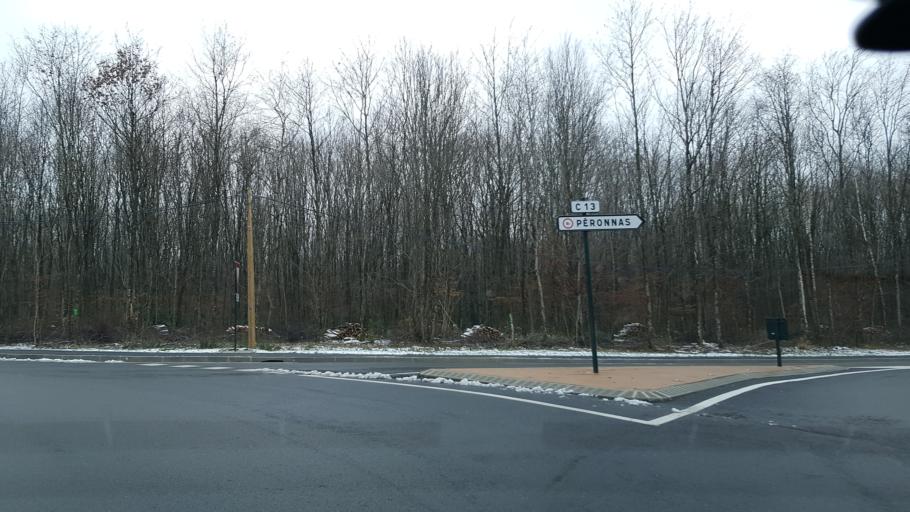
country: FR
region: Rhone-Alpes
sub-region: Departement de l'Ain
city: Peronnas
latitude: 46.1769
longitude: 5.2342
